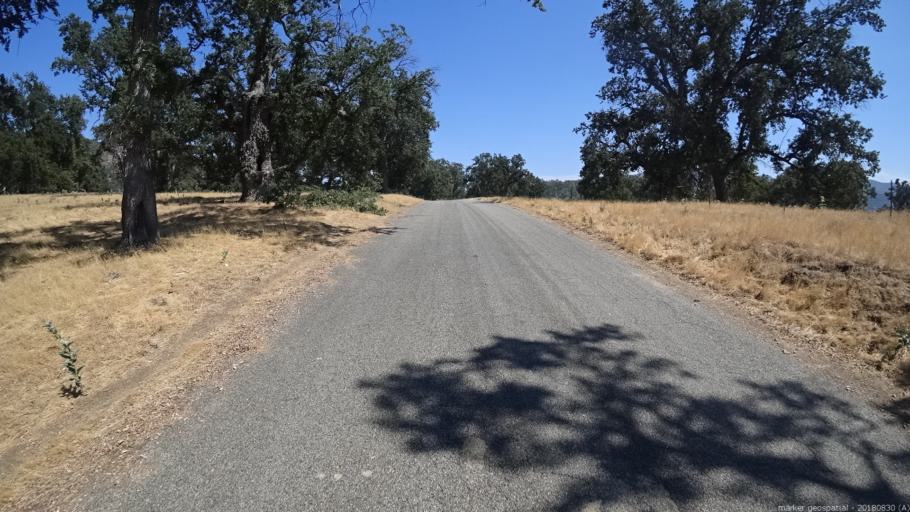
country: US
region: California
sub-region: Monterey County
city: Greenfield
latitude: 36.0838
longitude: -121.3999
